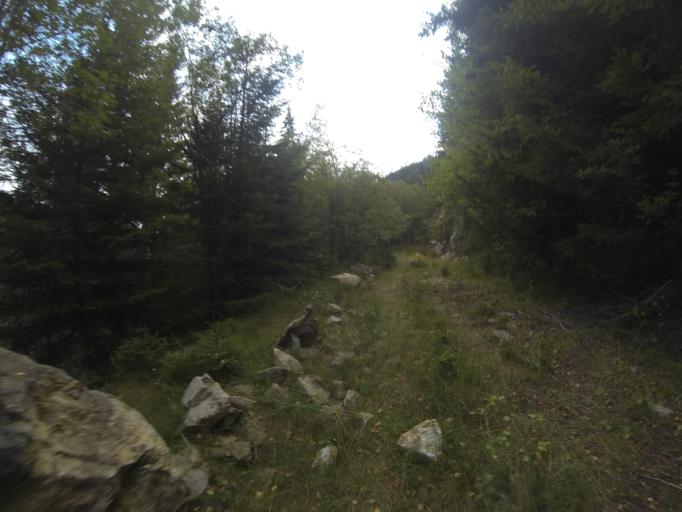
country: RO
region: Gorj
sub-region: Comuna Polovragi
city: Polovragi
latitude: 45.2766
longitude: 23.8316
